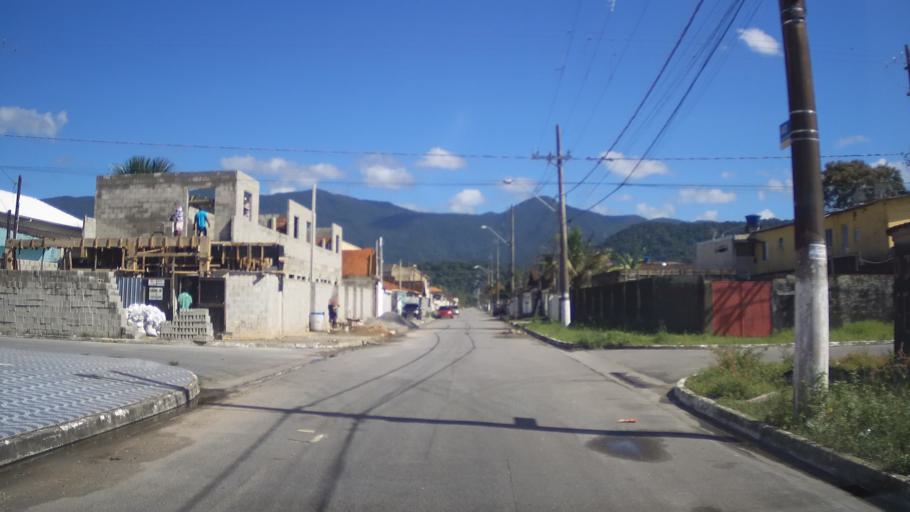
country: BR
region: Sao Paulo
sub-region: Mongagua
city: Mongagua
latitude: -24.0299
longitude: -46.5269
